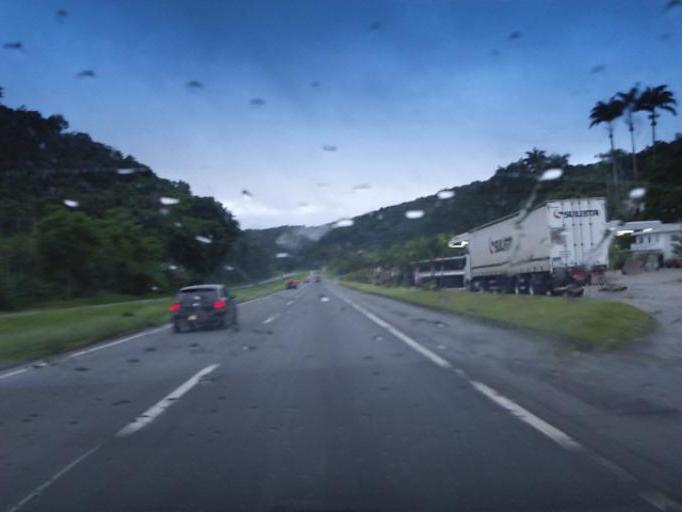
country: BR
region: Sao Paulo
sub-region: Miracatu
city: Miracatu
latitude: -24.1978
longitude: -47.3670
